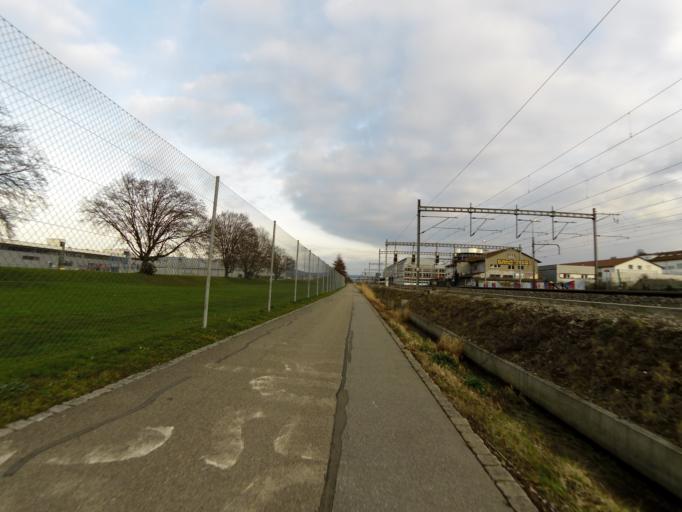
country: CH
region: Zurich
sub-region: Bezirk Dietikon
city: Schlieren / Boden
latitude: 47.3986
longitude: 8.4642
